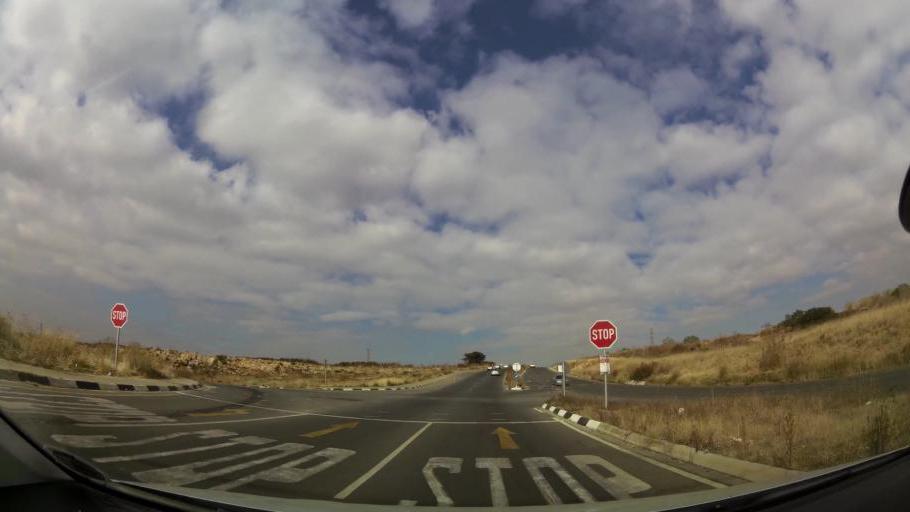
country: ZA
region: Gauteng
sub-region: City of Johannesburg Metropolitan Municipality
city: Roodepoort
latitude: -26.2054
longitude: 27.9046
